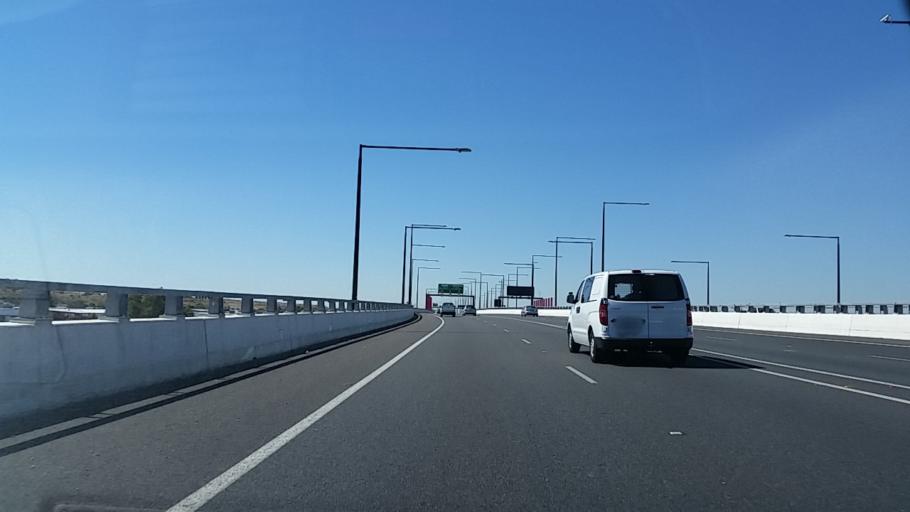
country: AU
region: South Australia
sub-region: Charles Sturt
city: Woodville North
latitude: -34.8431
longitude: 138.5641
